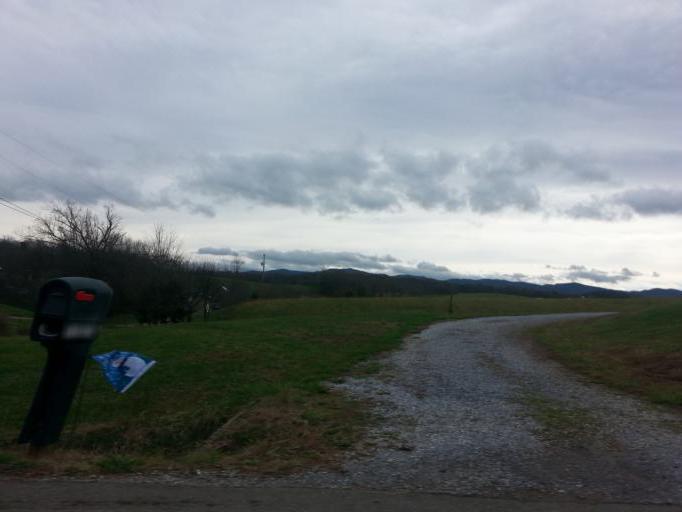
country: US
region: Tennessee
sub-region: Greene County
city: Mosheim
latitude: 36.0591
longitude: -82.9767
